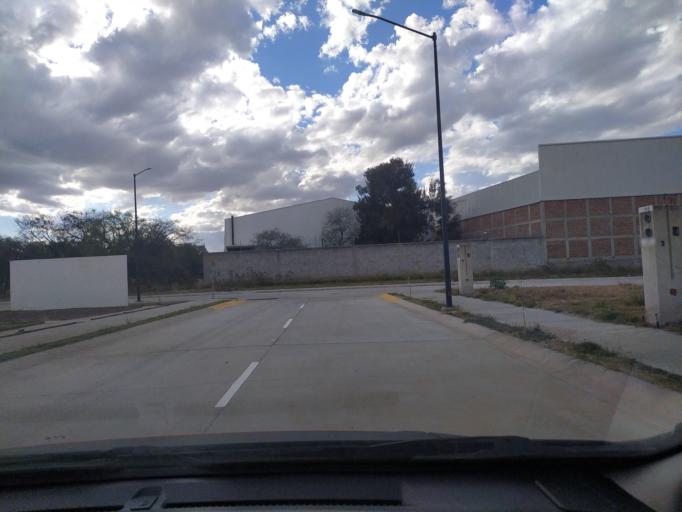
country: LA
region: Oudomxai
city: Muang La
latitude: 21.0246
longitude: 101.8246
